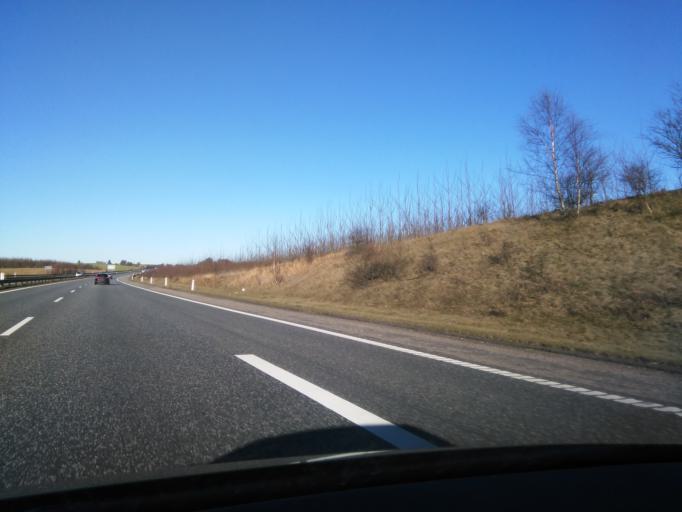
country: DK
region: Central Jutland
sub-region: Arhus Kommune
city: Trige
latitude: 56.3167
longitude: 10.1193
